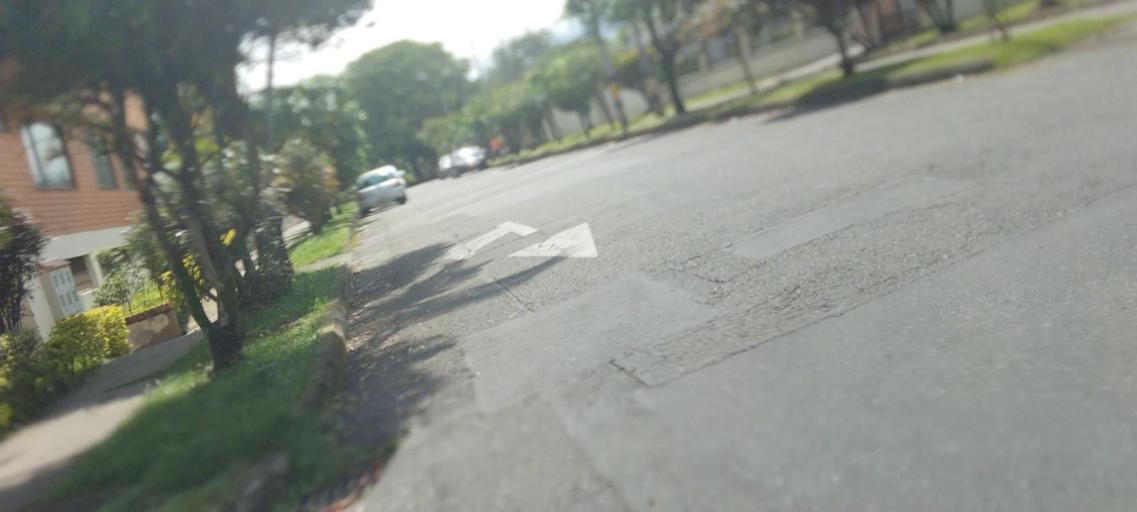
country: CO
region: Antioquia
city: Medellin
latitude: 6.2345
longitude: -75.5905
